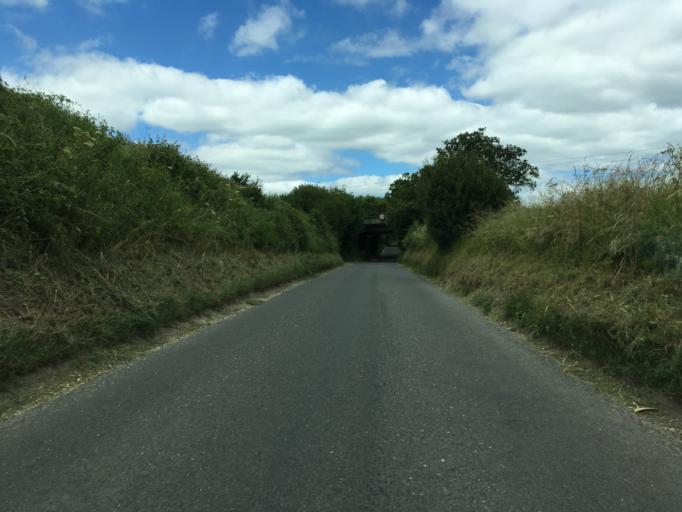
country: GB
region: England
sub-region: Hampshire
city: Overton
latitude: 51.2381
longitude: -1.3501
